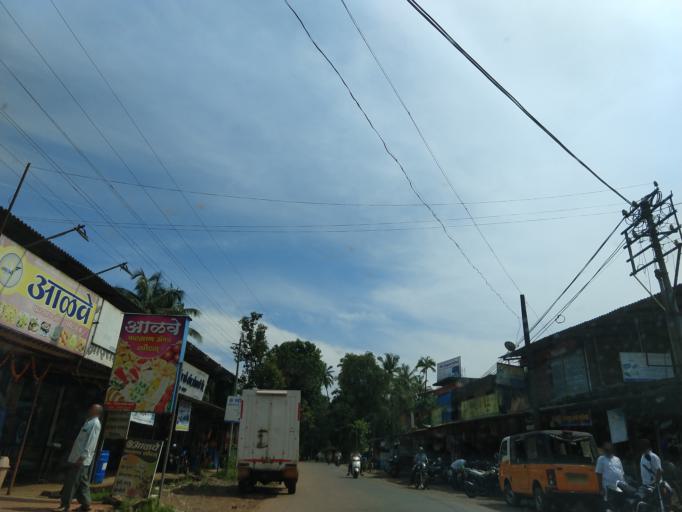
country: IN
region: Maharashtra
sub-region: Sindhudurg
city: Savantvadi
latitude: 15.9706
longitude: 73.7733
